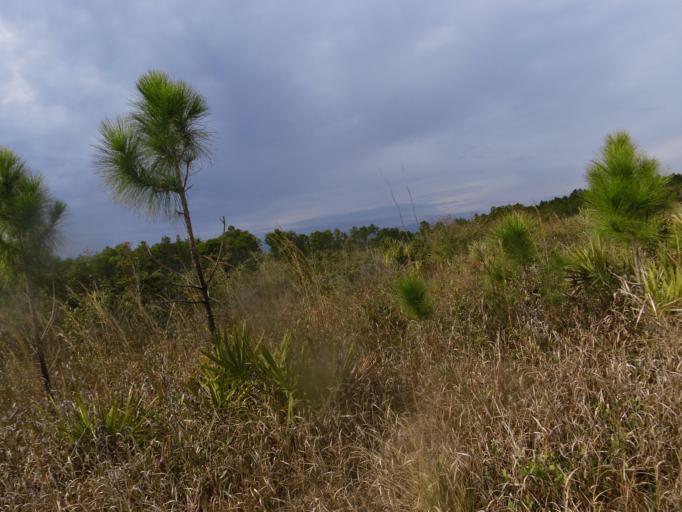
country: US
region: Florida
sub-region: Duval County
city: Atlantic Beach
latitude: 30.4726
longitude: -81.4906
